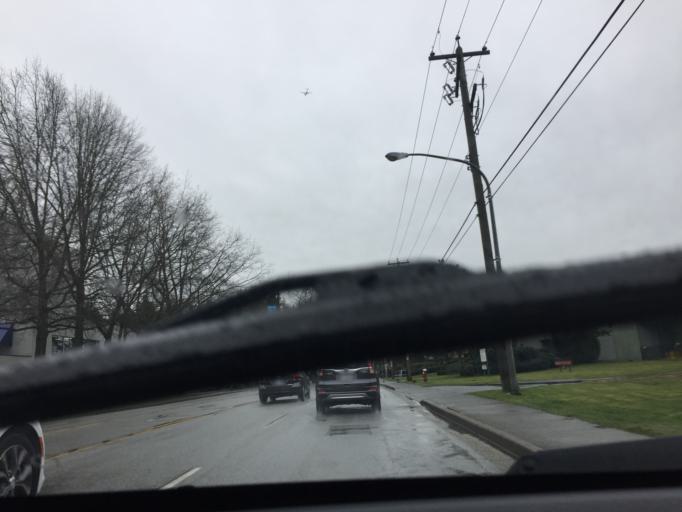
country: CA
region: British Columbia
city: Richmond
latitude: 49.1680
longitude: -123.1478
